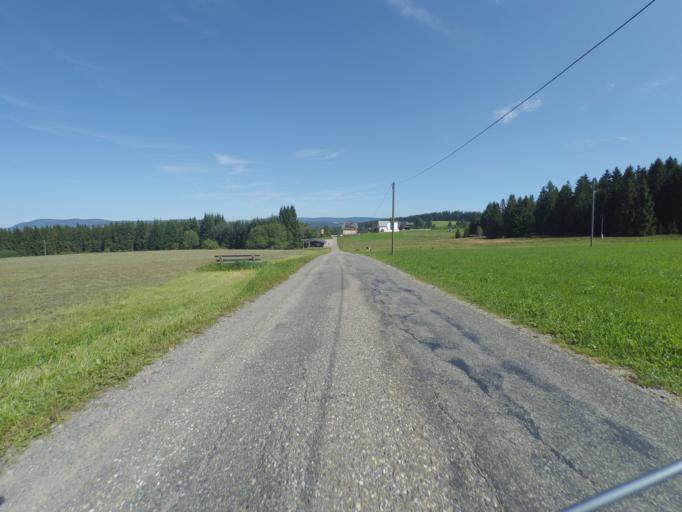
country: DE
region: Baden-Wuerttemberg
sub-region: Freiburg Region
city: Sankt Margen
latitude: 47.9687
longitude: 8.1225
